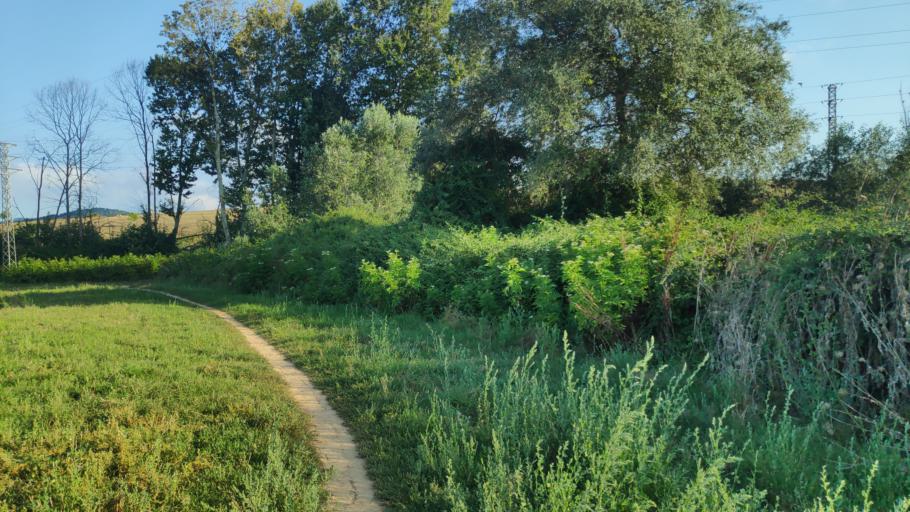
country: ES
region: Catalonia
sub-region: Provincia de Barcelona
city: Cerdanyola del Valles
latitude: 41.4937
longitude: 2.1204
